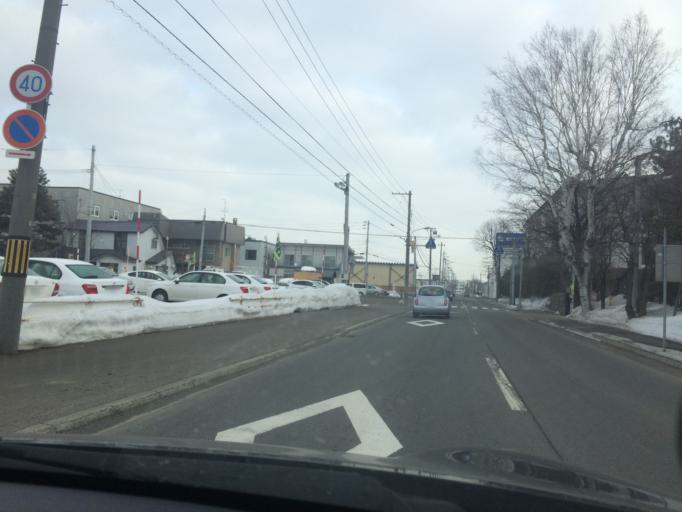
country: JP
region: Hokkaido
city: Sapporo
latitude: 43.0718
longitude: 141.3846
